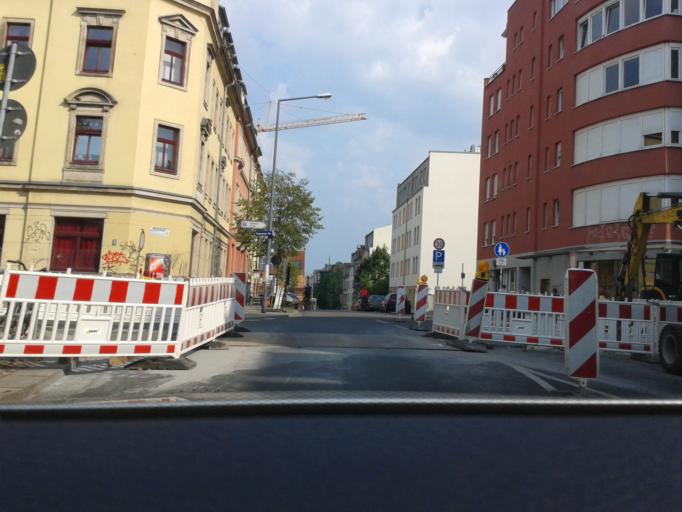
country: DE
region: Saxony
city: Albertstadt
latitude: 51.0690
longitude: 13.7588
